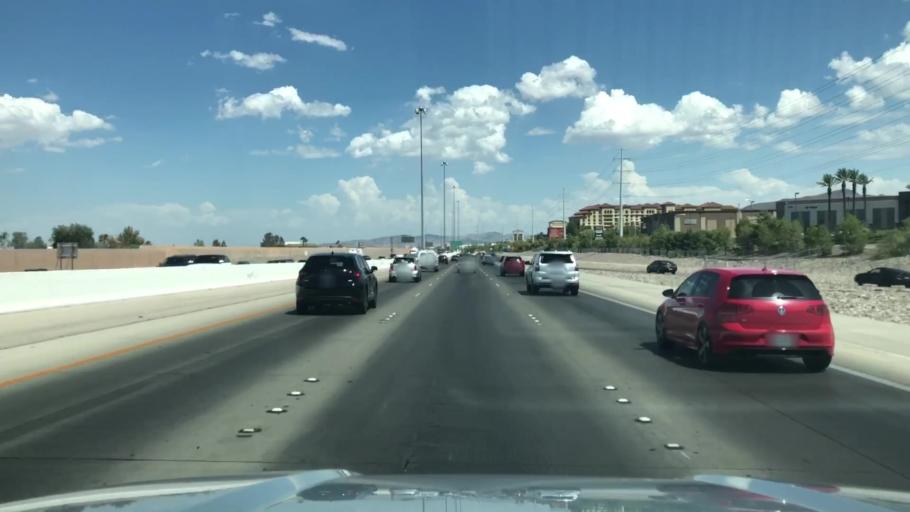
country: US
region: Nevada
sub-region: Clark County
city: Whitney
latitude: 36.0234
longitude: -115.0980
